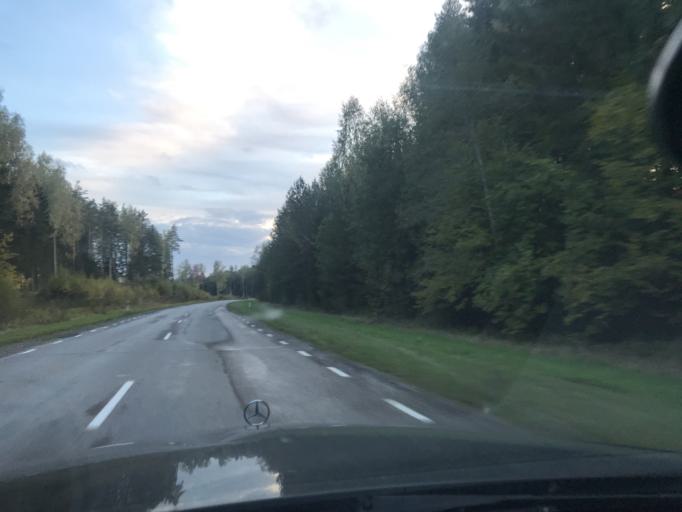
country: EE
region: Valgamaa
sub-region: Torva linn
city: Torva
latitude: 57.9953
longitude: 26.0758
